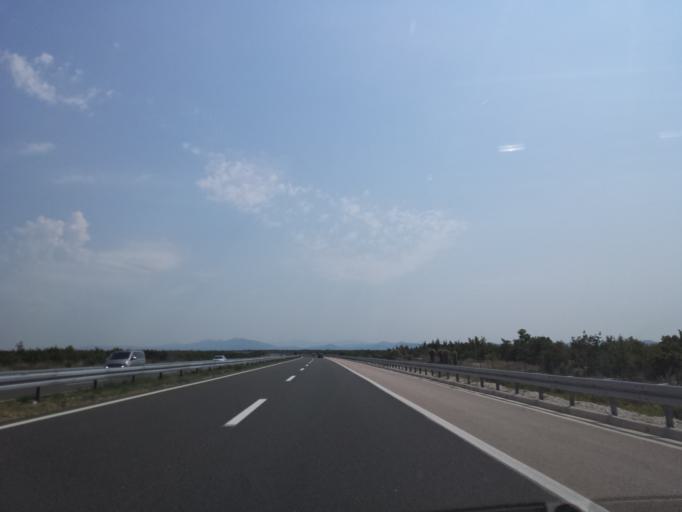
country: HR
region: Sibensko-Kniniska
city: Zaton
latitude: 43.8753
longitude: 15.8031
